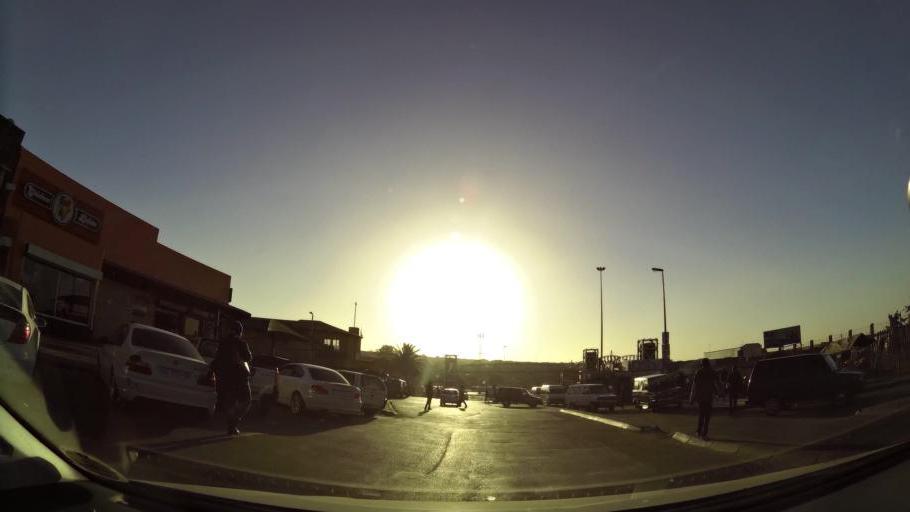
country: ZA
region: Gauteng
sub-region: Ekurhuleni Metropolitan Municipality
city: Tembisa
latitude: -26.0211
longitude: 28.2008
